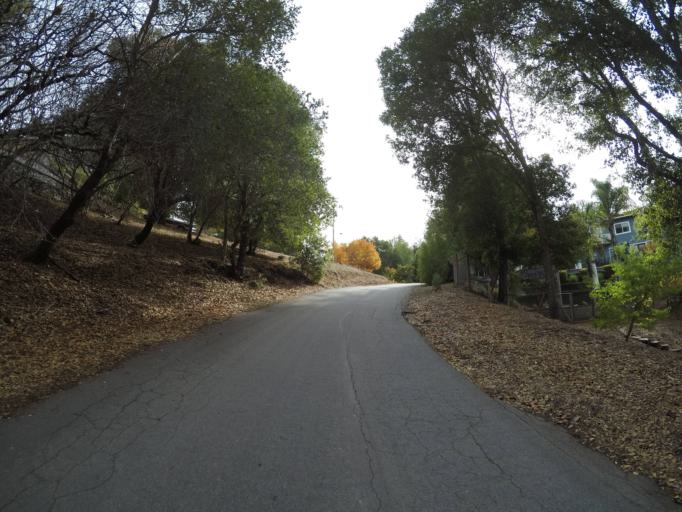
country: US
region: California
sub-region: Santa Cruz County
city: Scotts Valley
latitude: 37.0548
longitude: -121.9916
